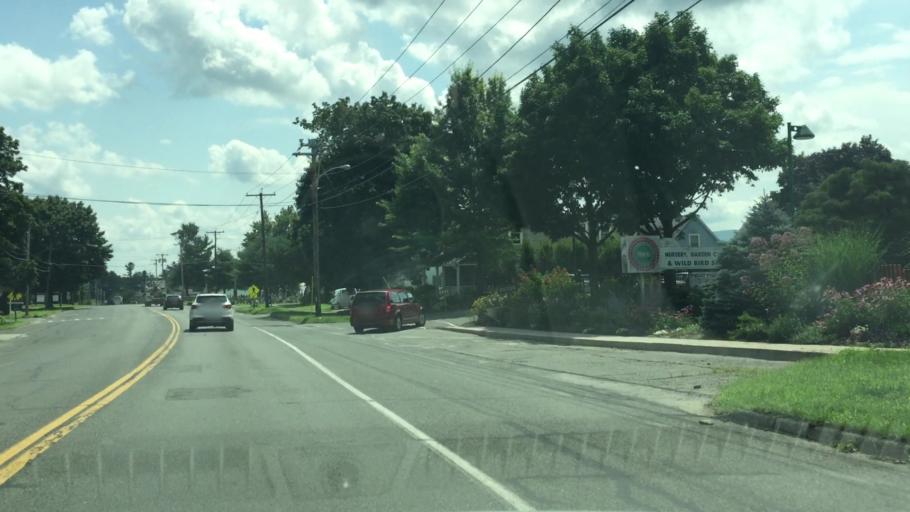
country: US
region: Massachusetts
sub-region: Berkshire County
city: Great Barrington
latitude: 42.1850
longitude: -73.3645
